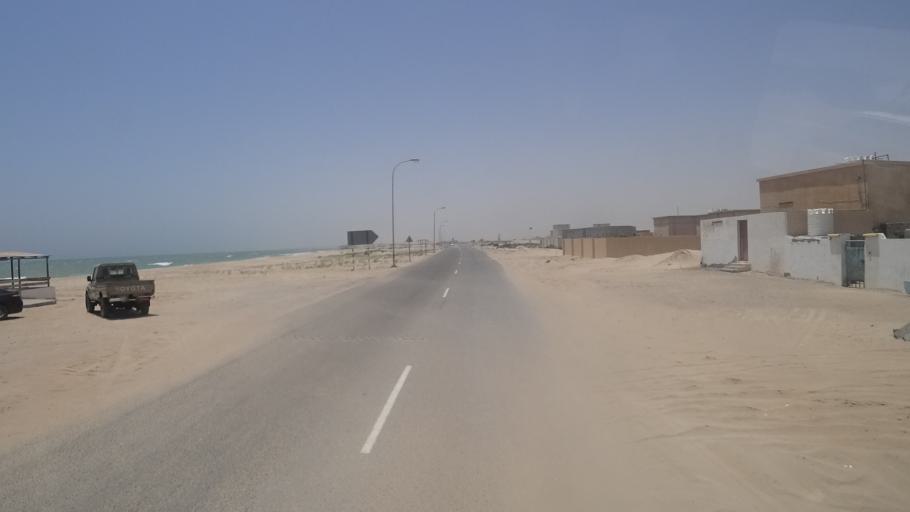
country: OM
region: Ash Sharqiyah
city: Sur
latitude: 22.0792
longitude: 59.6827
